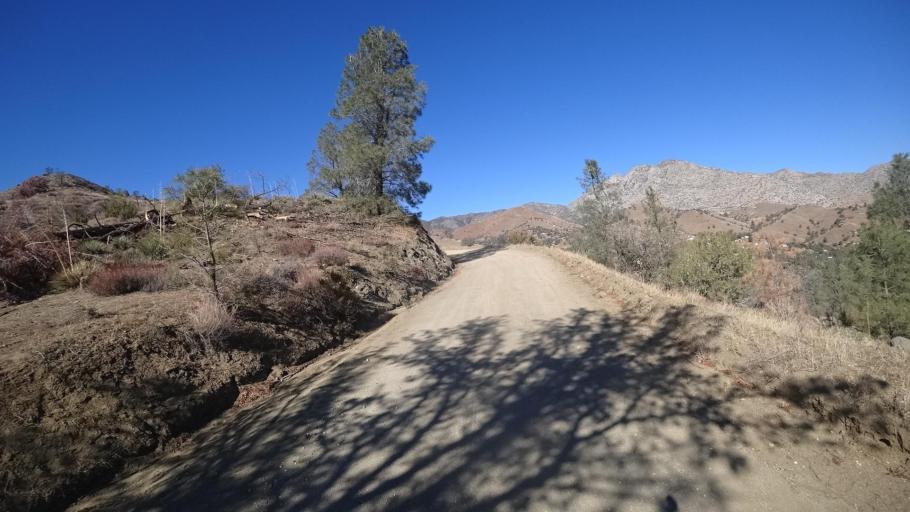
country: US
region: California
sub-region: Kern County
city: Wofford Heights
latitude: 35.7046
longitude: -118.4776
